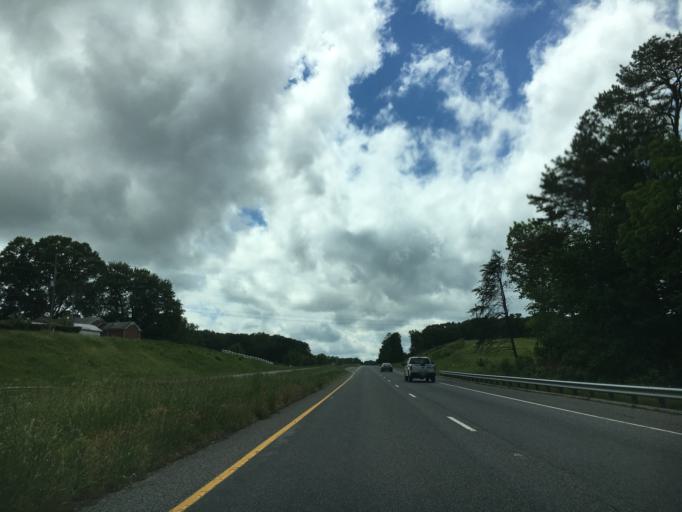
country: US
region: Virginia
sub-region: Mecklenburg County
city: Boydton
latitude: 36.6532
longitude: -78.4641
